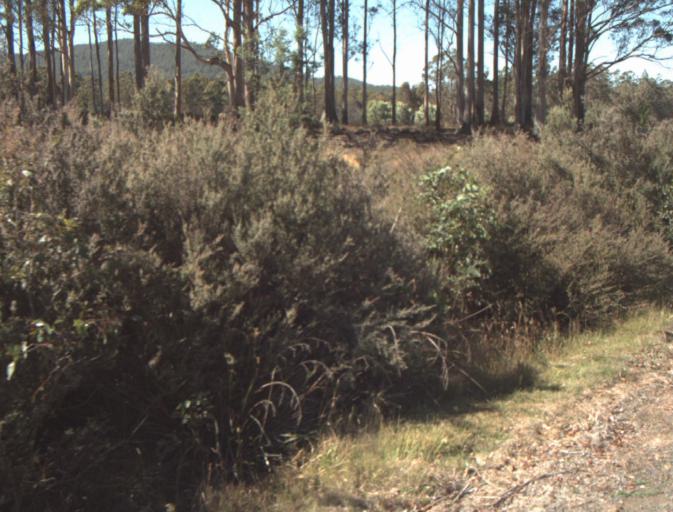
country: AU
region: Tasmania
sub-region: Launceston
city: Newstead
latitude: -41.3730
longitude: 147.2975
